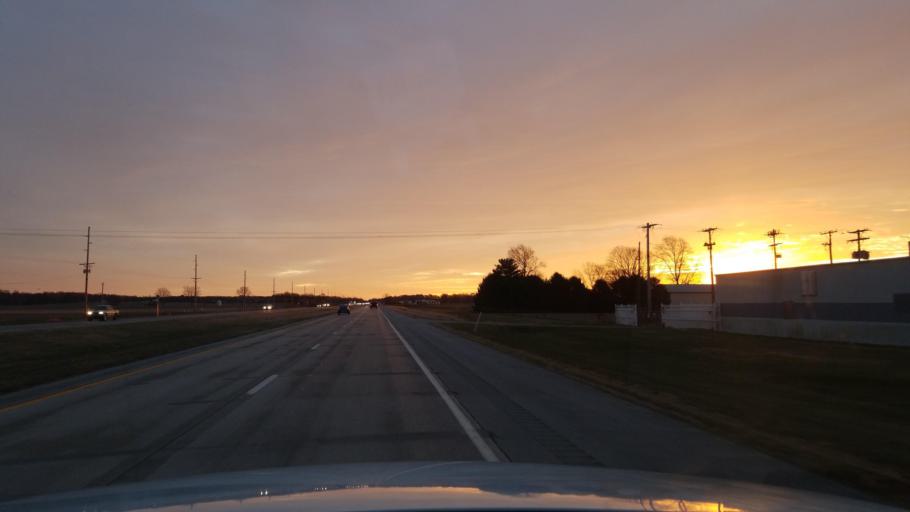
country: US
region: Indiana
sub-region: Posey County
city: Mount Vernon
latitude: 37.9421
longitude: -87.7840
